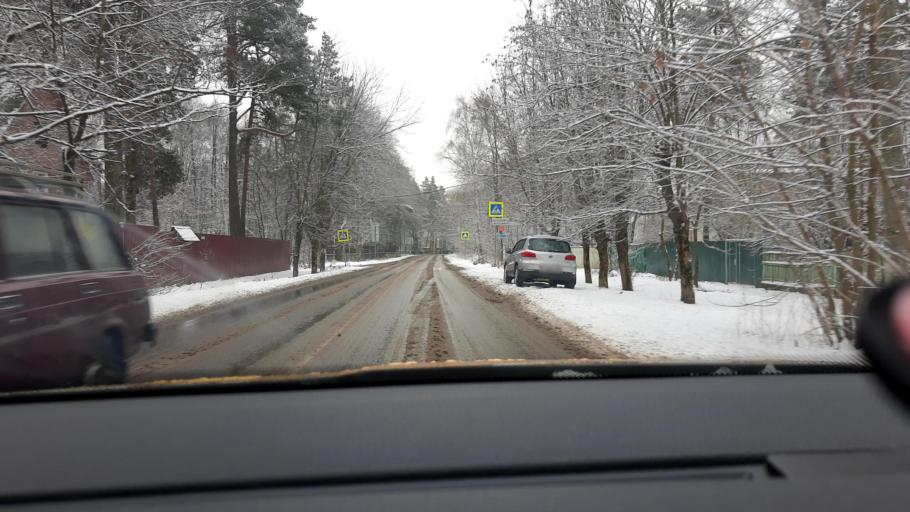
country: RU
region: Moskovskaya
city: Mamontovka
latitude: 55.9766
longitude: 37.8214
